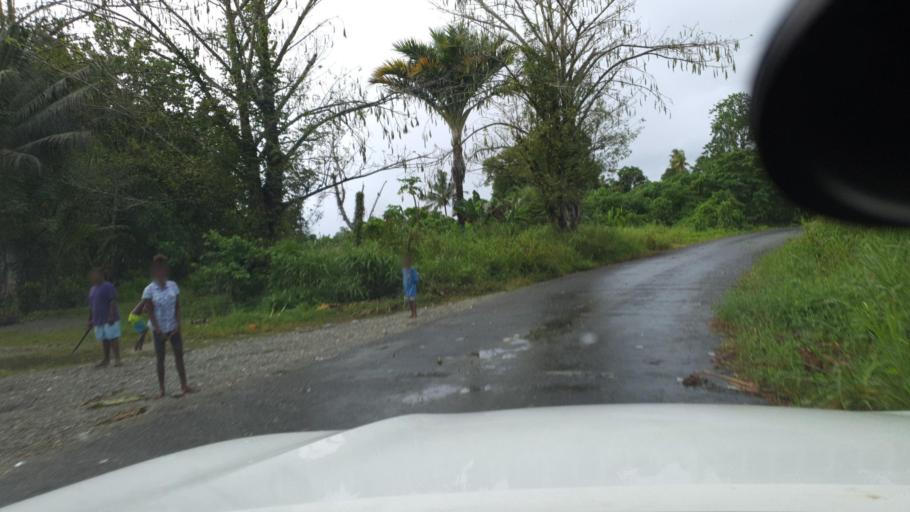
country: SB
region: Guadalcanal
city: Honiara
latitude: -9.4666
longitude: 160.3592
